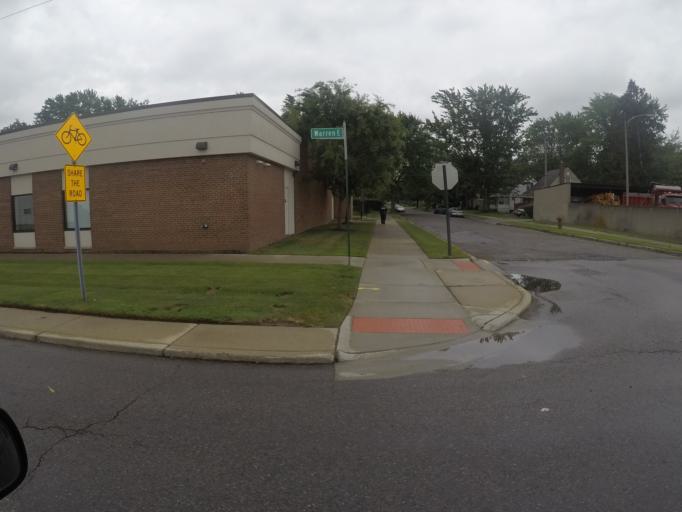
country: US
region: Michigan
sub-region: Wayne County
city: Harper Woods
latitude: 42.4099
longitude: -82.9195
